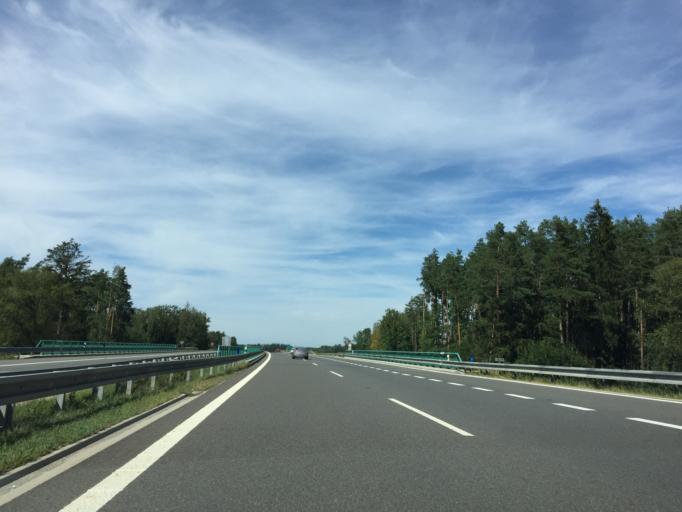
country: CZ
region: Jihocesky
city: Sobeslav
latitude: 49.2271
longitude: 14.7282
